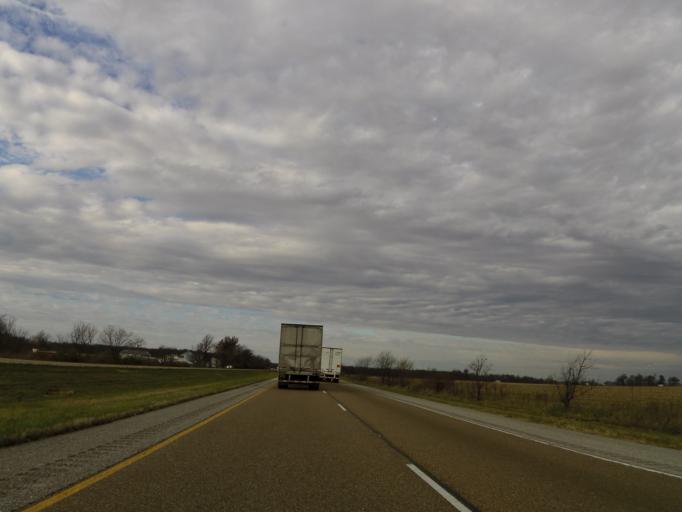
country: US
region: Illinois
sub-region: Washington County
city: Nashville
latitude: 38.3914
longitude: -89.2844
